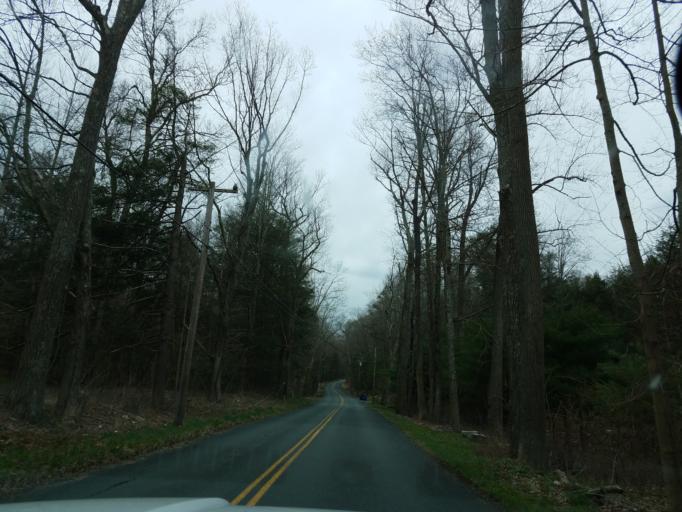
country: US
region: Connecticut
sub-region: Tolland County
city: Somers
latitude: 41.9800
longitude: -72.4213
